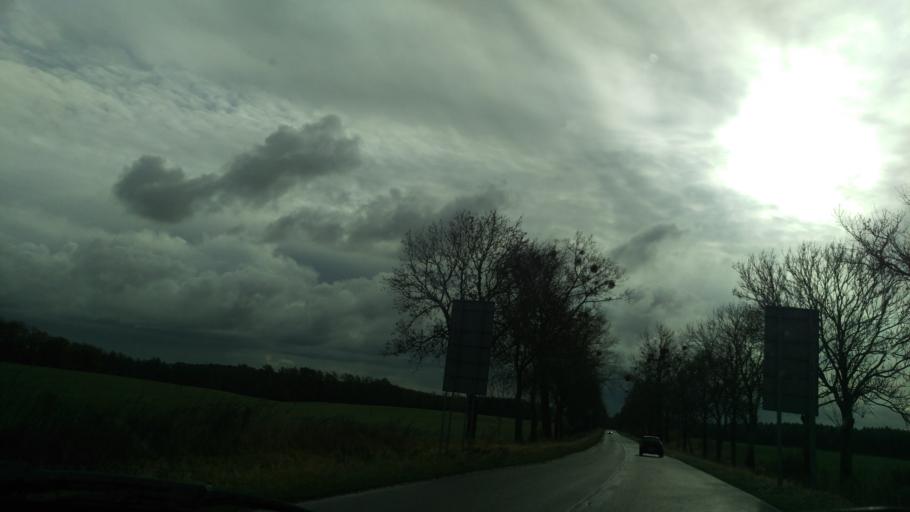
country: PL
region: West Pomeranian Voivodeship
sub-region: Powiat gryficki
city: Gryfice
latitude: 53.8679
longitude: 15.2173
